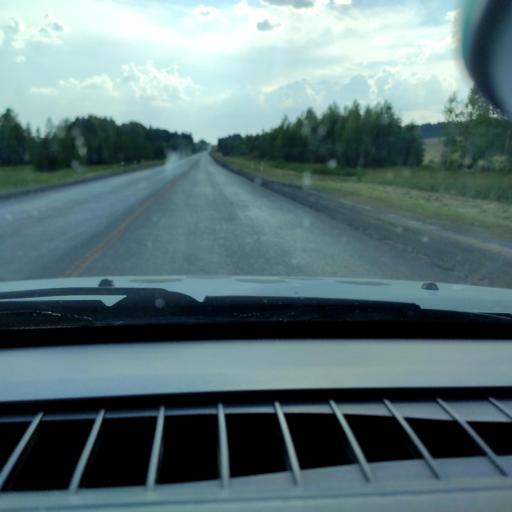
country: RU
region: Udmurtiya
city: Debesy
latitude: 57.7015
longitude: 54.0530
